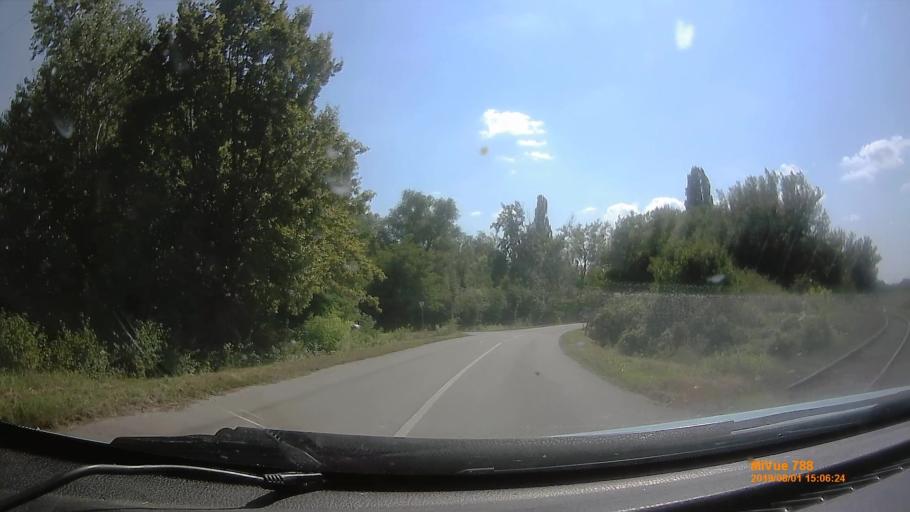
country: HU
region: Baranya
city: Sellye
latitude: 45.8651
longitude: 17.8402
